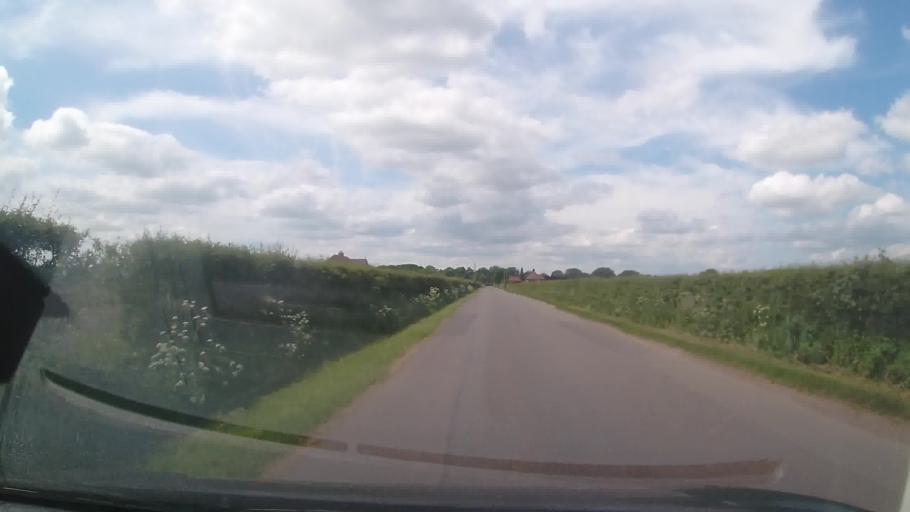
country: GB
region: England
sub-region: Shropshire
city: Shawbury
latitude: 52.7975
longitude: -2.5811
